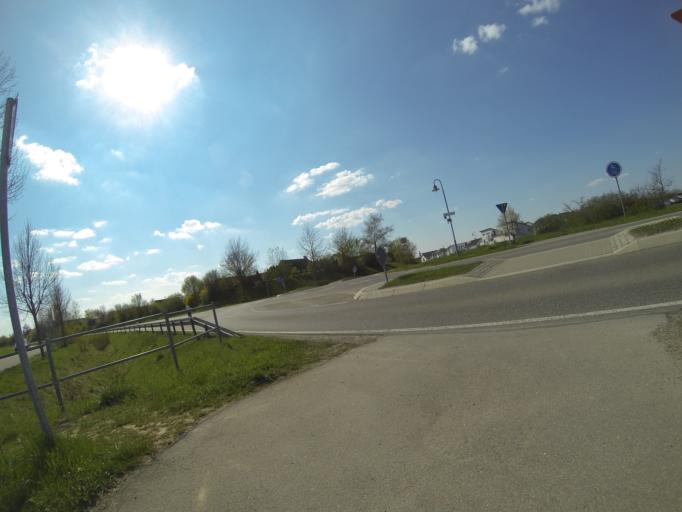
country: DE
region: Baden-Wuerttemberg
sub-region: Tuebingen Region
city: Laupheim
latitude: 48.2273
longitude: 9.9023
